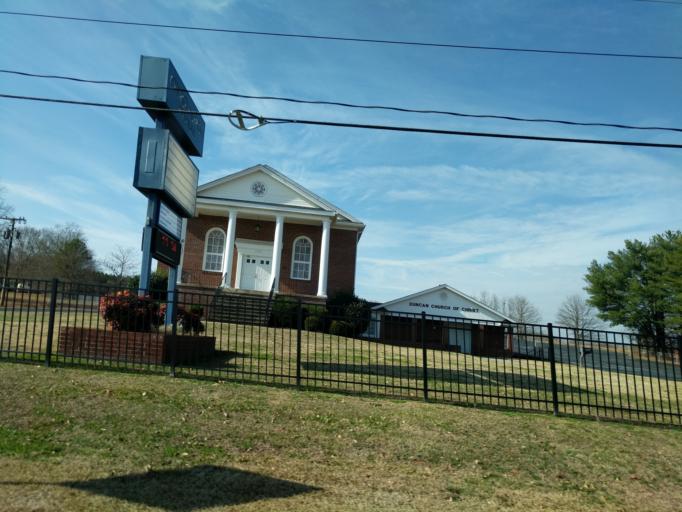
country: US
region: South Carolina
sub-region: Spartanburg County
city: Duncan
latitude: 34.9039
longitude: -82.1362
